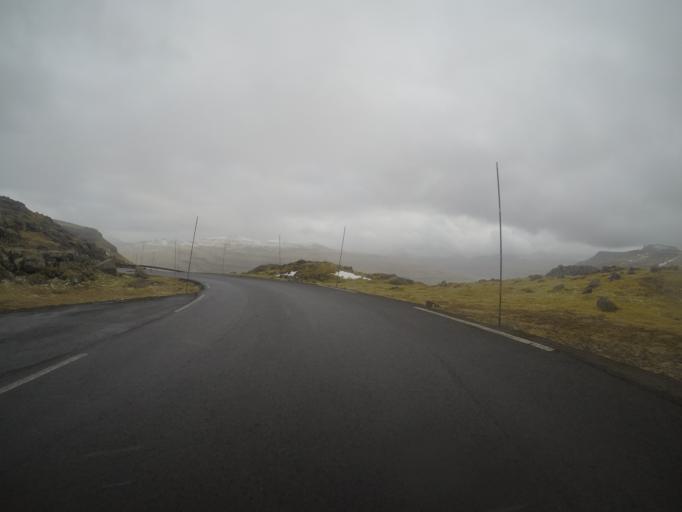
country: FO
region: Streymoy
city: Kollafjordhur
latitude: 62.0825
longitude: -6.9427
